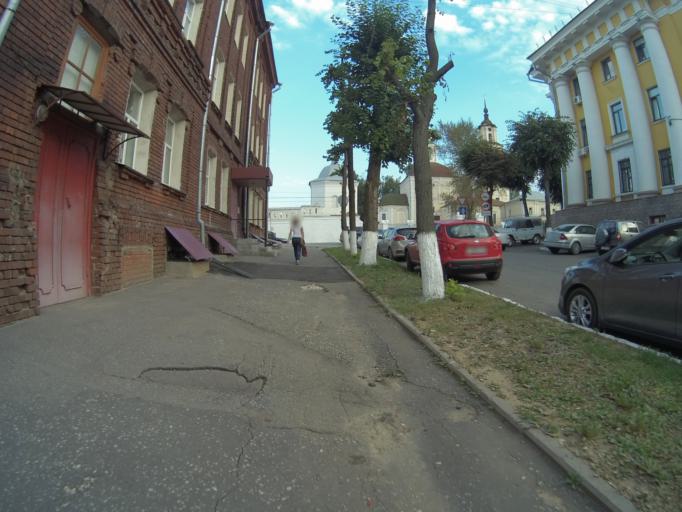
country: RU
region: Vladimir
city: Vladimir
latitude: 56.1316
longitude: 40.4114
